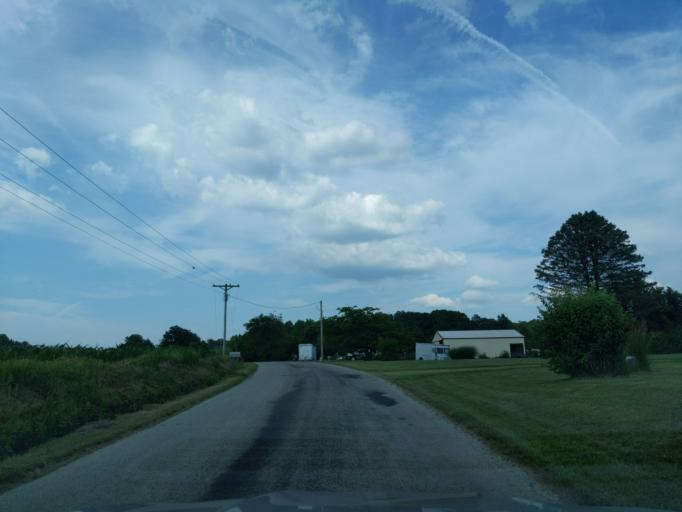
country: US
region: Indiana
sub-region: Ripley County
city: Osgood
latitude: 39.1931
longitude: -85.3931
